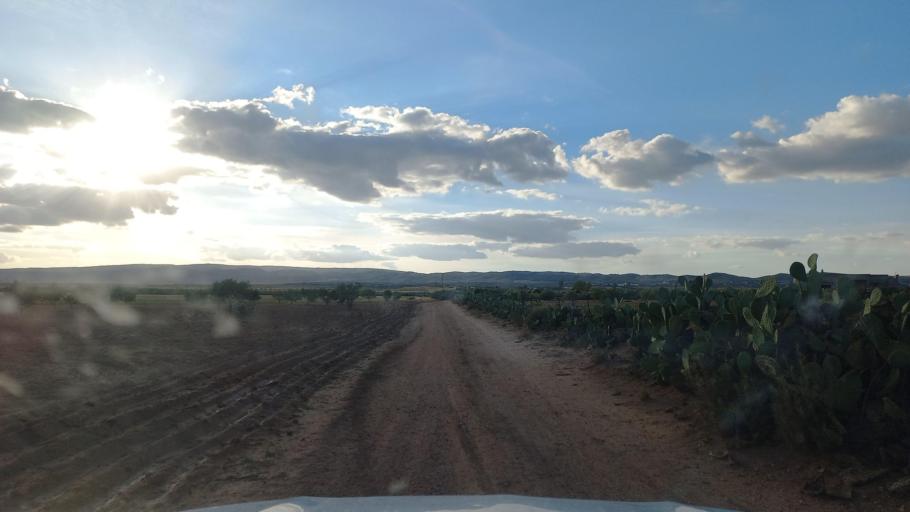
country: TN
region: Al Qasrayn
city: Sbiba
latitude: 35.3518
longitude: 9.0357
